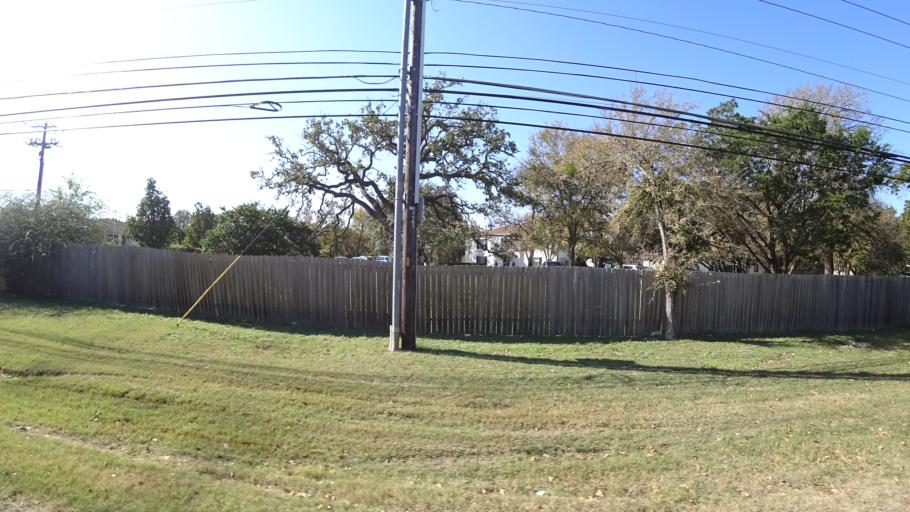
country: US
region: Texas
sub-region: Travis County
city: Barton Creek
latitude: 30.2330
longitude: -97.8571
